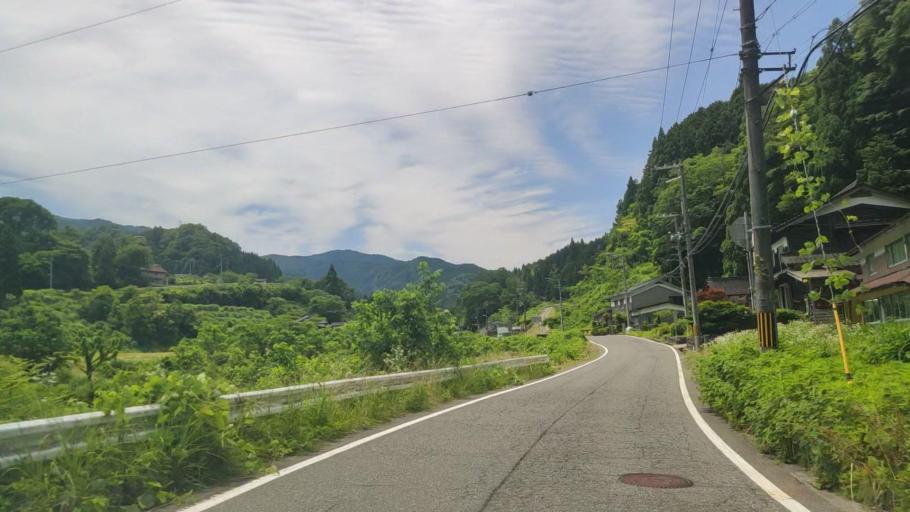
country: JP
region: Tottori
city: Tottori
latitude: 35.4338
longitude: 134.5326
